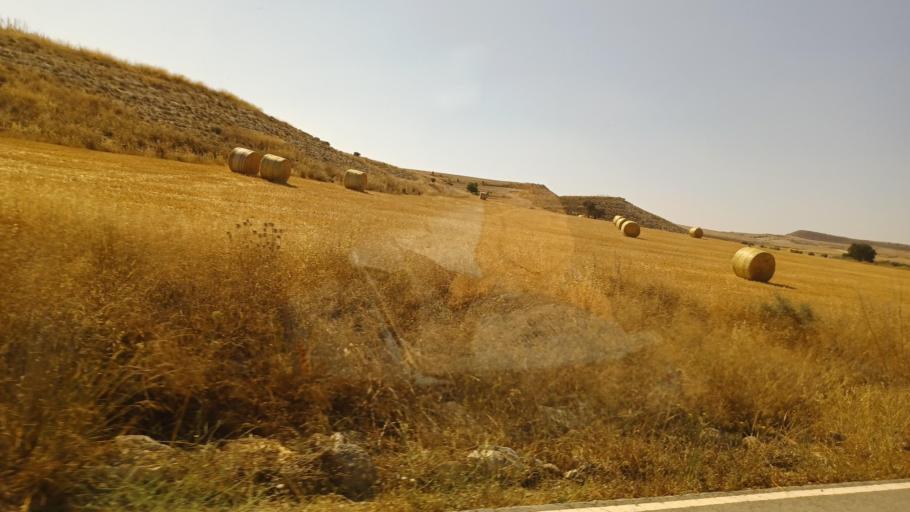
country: CY
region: Larnaka
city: Athienou
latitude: 35.0387
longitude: 33.5106
